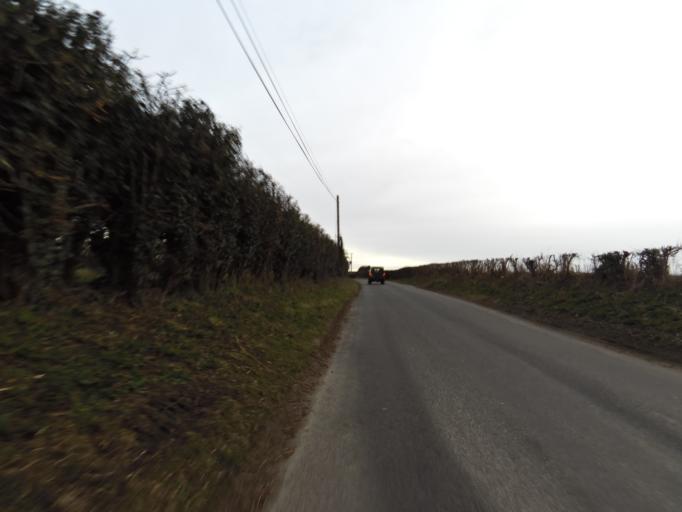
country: GB
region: England
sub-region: Suffolk
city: Bramford
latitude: 52.0246
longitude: 1.1049
